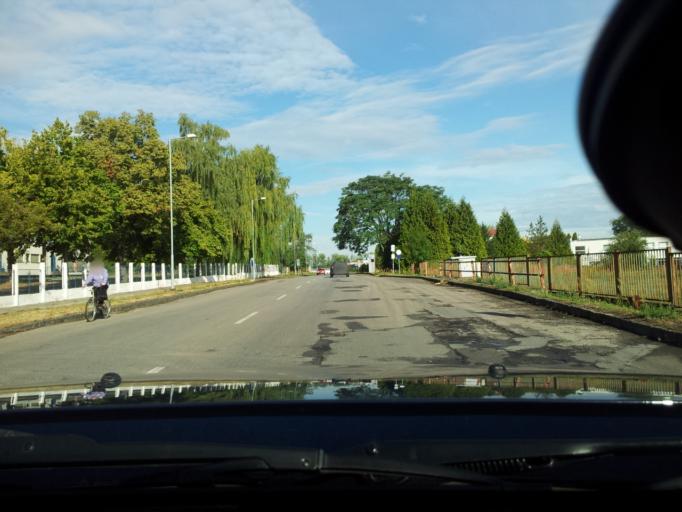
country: SK
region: Kosicky
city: Michalovce
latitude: 48.7656
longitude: 21.9041
